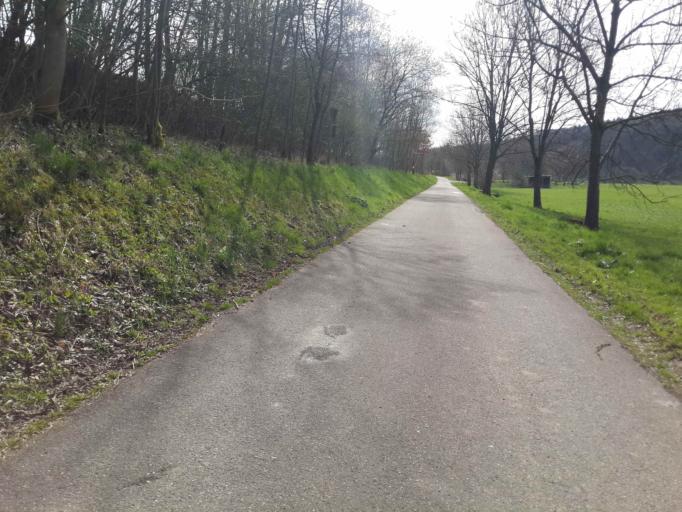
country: DE
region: Baden-Wuerttemberg
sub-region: Regierungsbezirk Stuttgart
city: Weissbach
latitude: 49.3543
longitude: 9.5737
